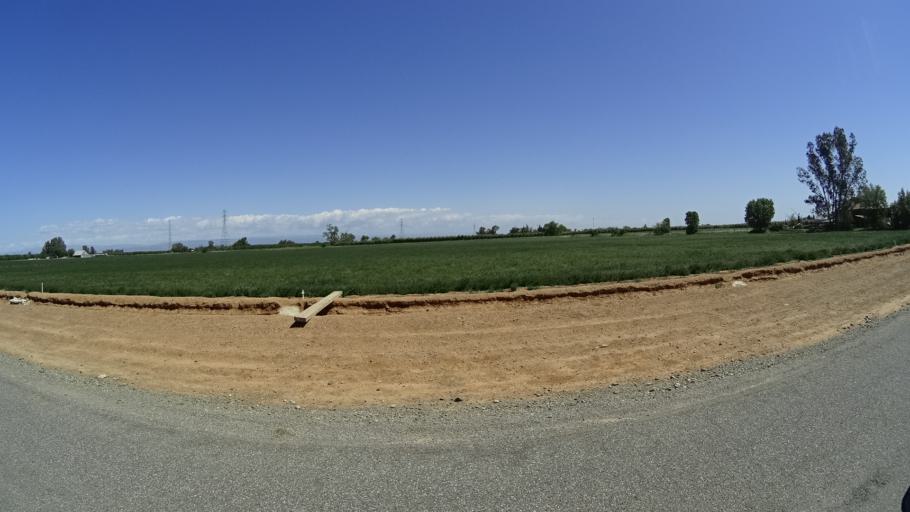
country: US
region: California
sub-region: Glenn County
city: Orland
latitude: 39.7934
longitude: -122.1785
